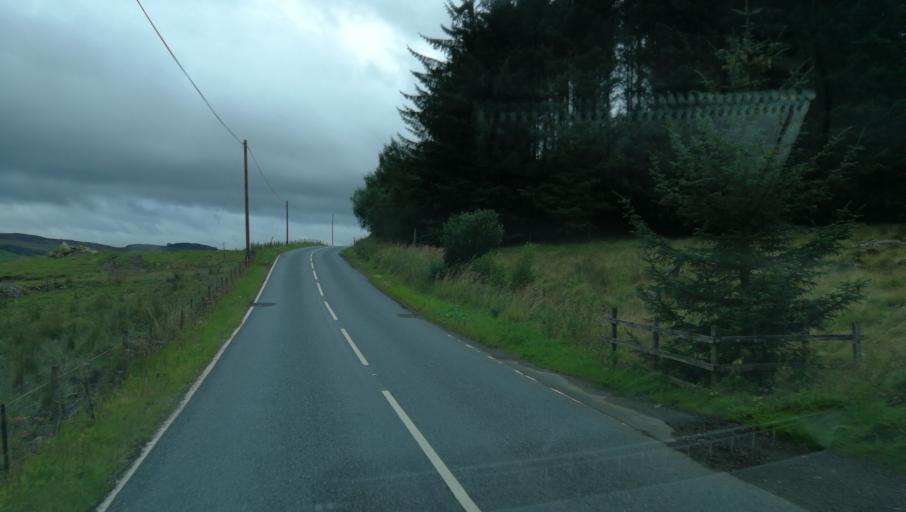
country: GB
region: Scotland
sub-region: Perth and Kinross
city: Blairgowrie
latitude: 56.7475
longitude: -3.4041
